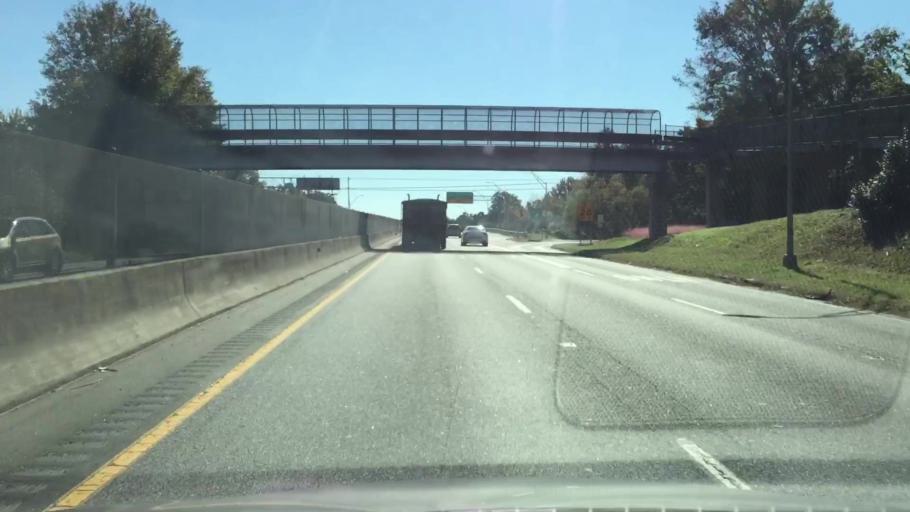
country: US
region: North Carolina
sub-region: Guilford County
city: Greensboro
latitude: 36.0659
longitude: -79.7667
